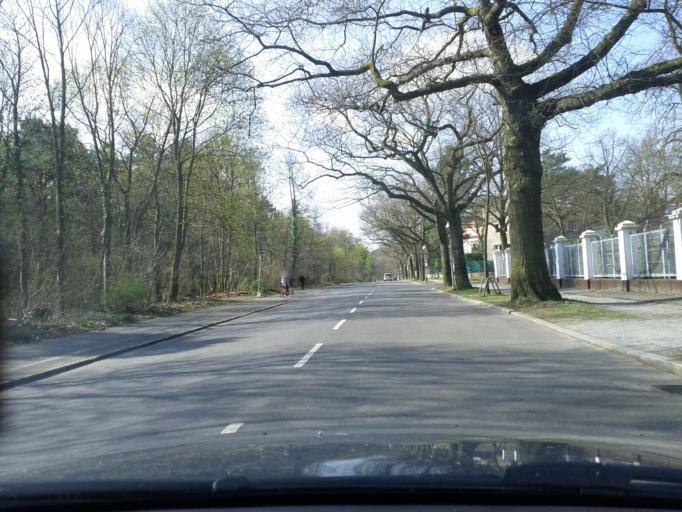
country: DE
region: Berlin
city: Westend
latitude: 52.5072
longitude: 13.2566
